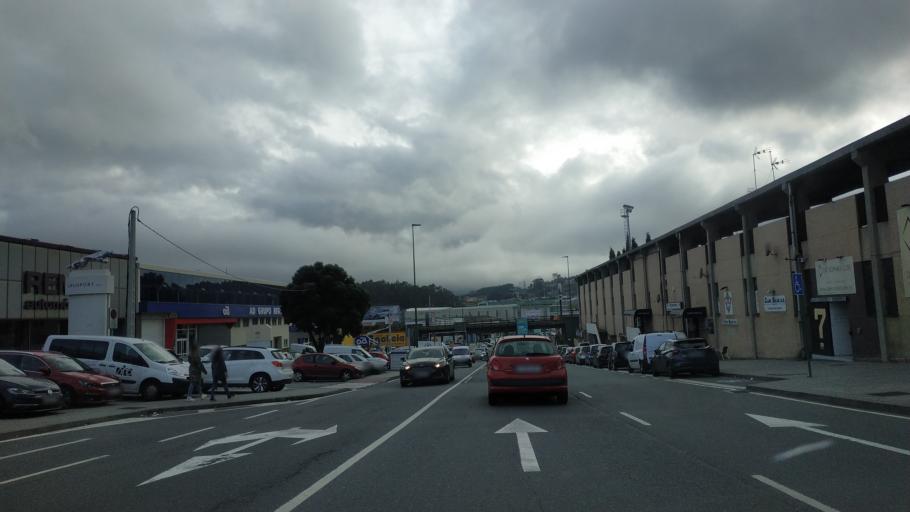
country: ES
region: Galicia
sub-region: Provincia da Coruna
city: A Coruna
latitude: 43.3522
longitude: -8.4225
